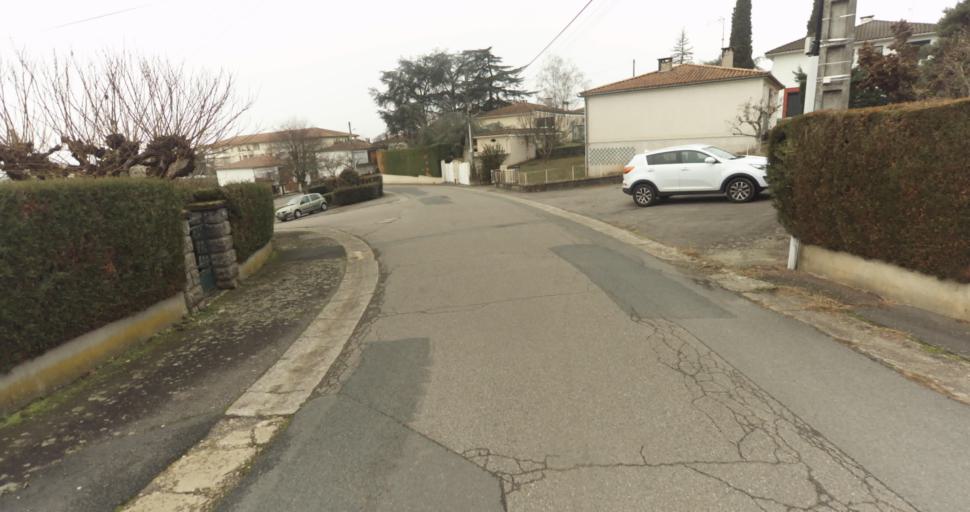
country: FR
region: Midi-Pyrenees
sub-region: Departement du Lot
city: Figeac
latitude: 44.6179
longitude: 2.0418
